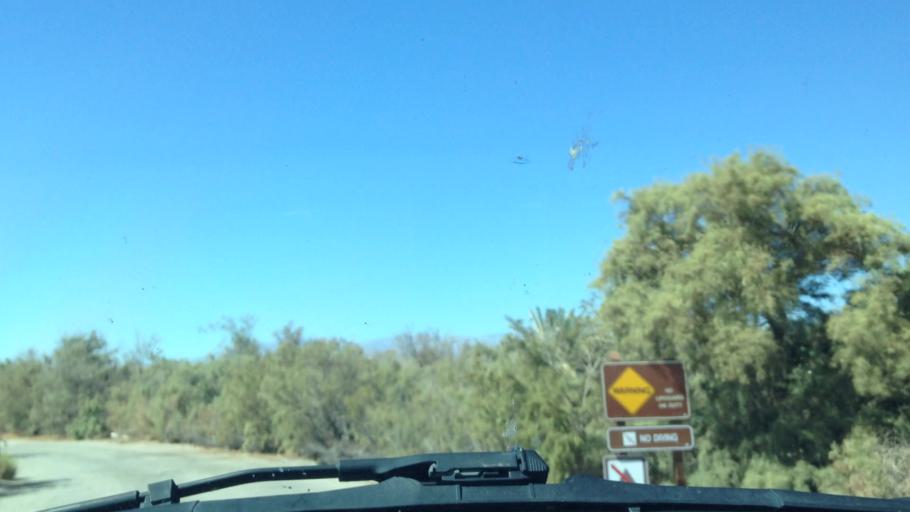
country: US
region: California
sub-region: Imperial County
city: Desert Shores
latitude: 33.5092
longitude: -115.9207
